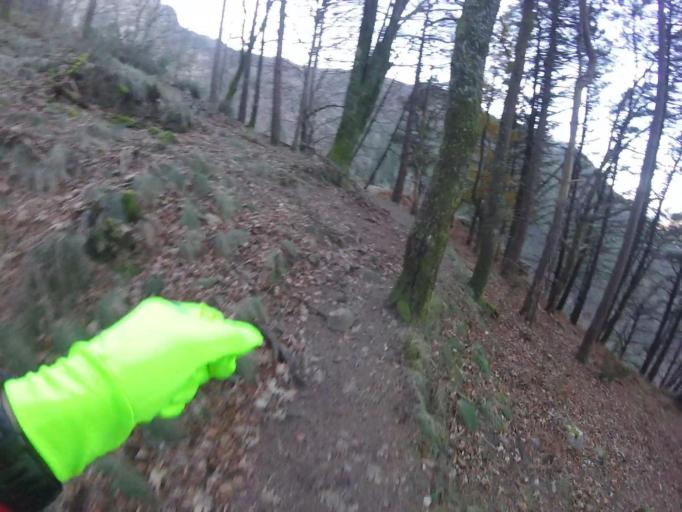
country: ES
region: Basque Country
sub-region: Provincia de Guipuzcoa
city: Irun
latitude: 43.2861
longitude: -1.7915
